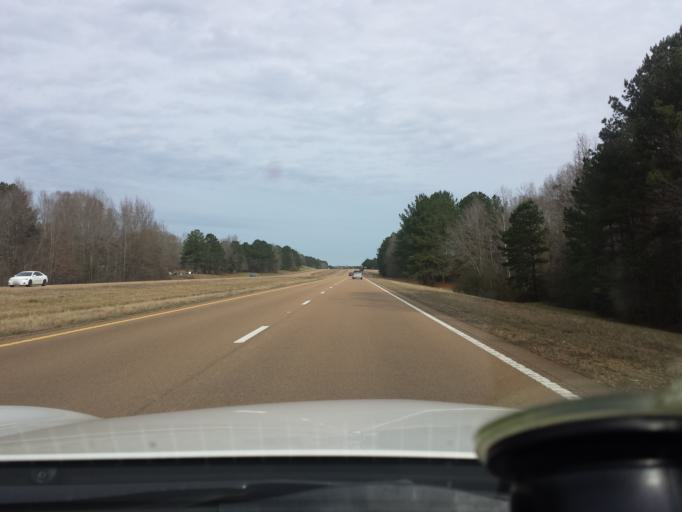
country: US
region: Mississippi
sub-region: Leake County
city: Carthage
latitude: 32.6150
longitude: -89.6936
